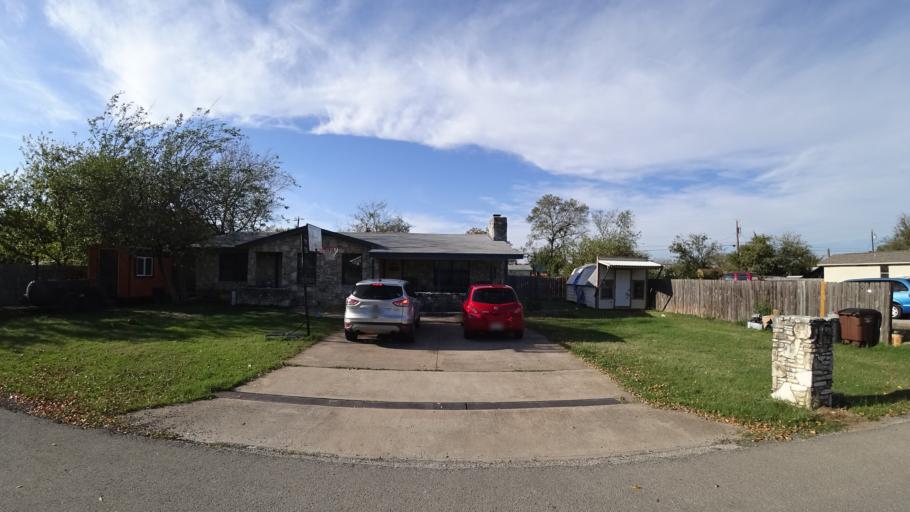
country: US
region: Texas
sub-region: Travis County
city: Wells Branch
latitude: 30.4720
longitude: -97.6865
